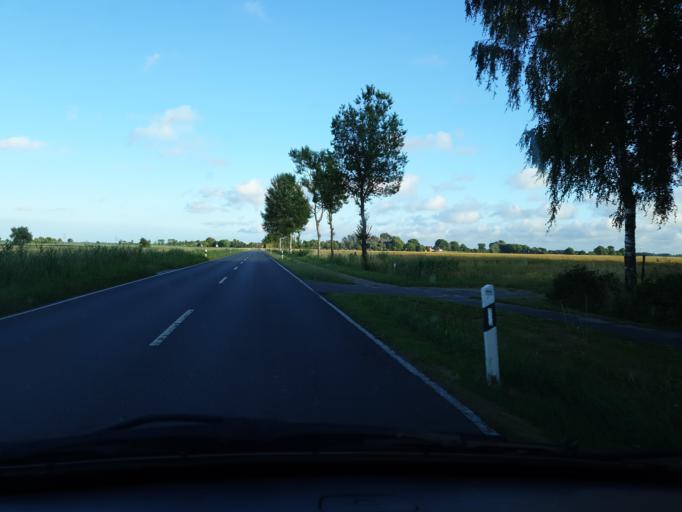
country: DE
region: Schleswig-Holstein
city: Wohrden
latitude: 54.1538
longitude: 9.0148
